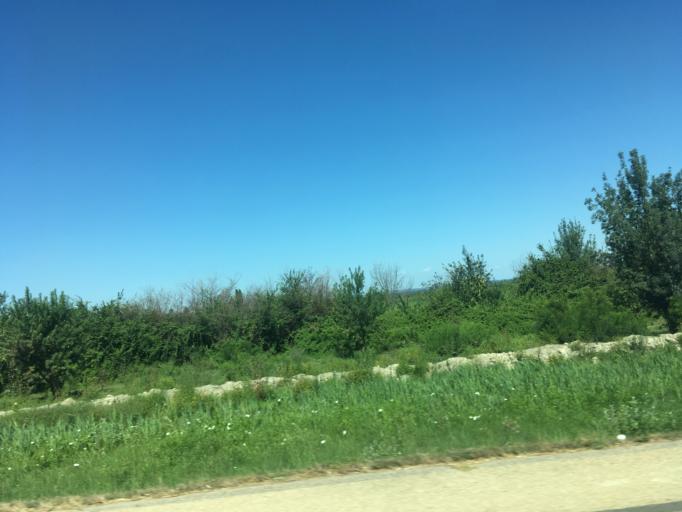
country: FR
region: Languedoc-Roussillon
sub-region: Departement du Gard
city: Saint-Gilles
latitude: 43.6144
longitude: 4.4811
